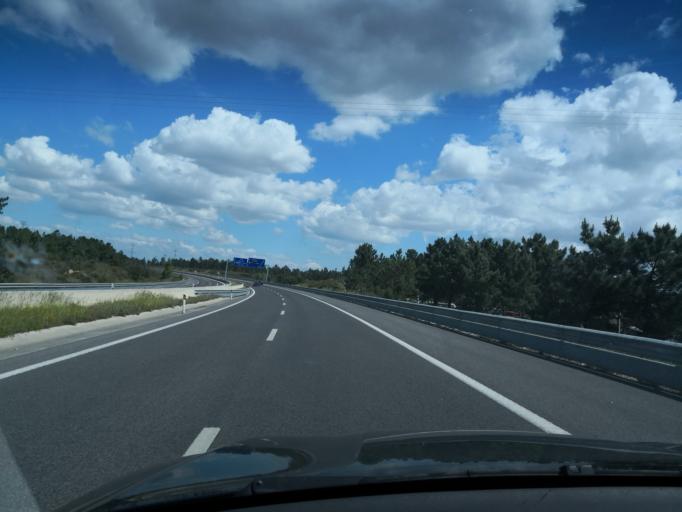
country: PT
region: Setubal
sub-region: Seixal
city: Corroios
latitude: 38.6070
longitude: -9.1478
